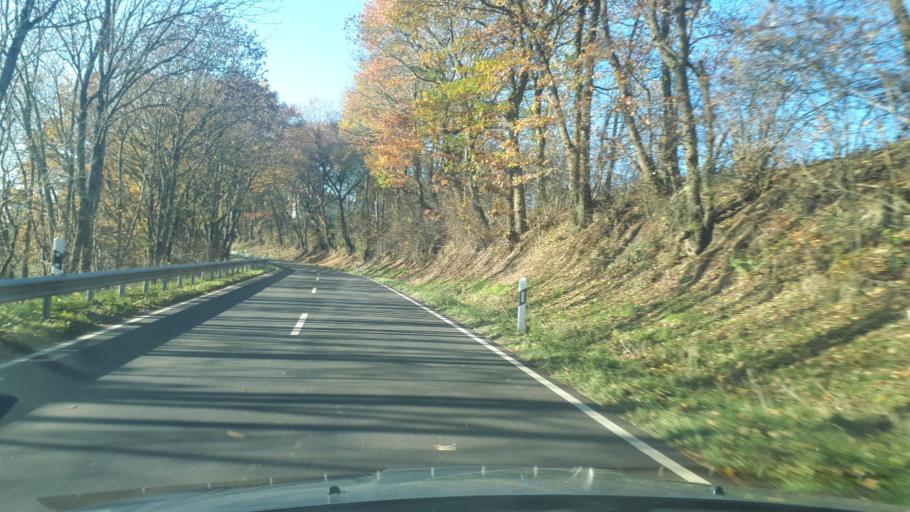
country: DE
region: Rheinland-Pfalz
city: Weiler
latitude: 50.1553
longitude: 7.0927
